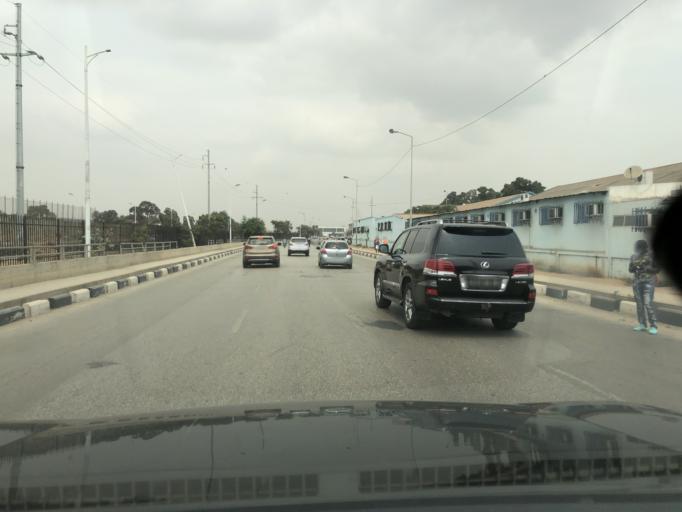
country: AO
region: Luanda
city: Luanda
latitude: -8.8347
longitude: 13.2548
